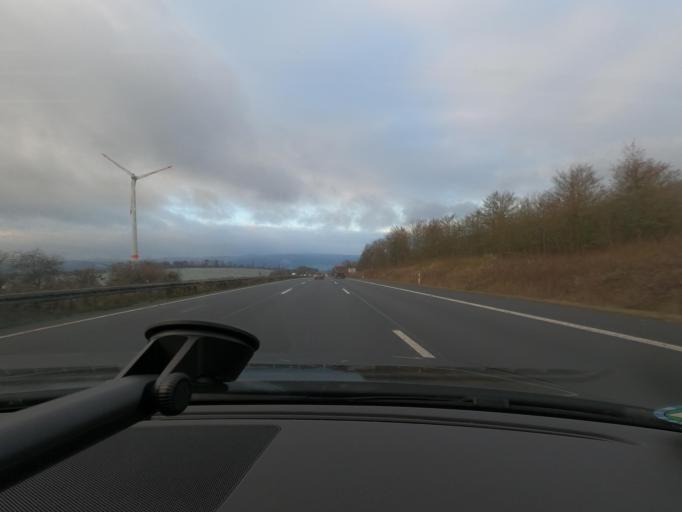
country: DE
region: Lower Saxony
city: Juhnde
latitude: 51.4074
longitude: 9.8131
